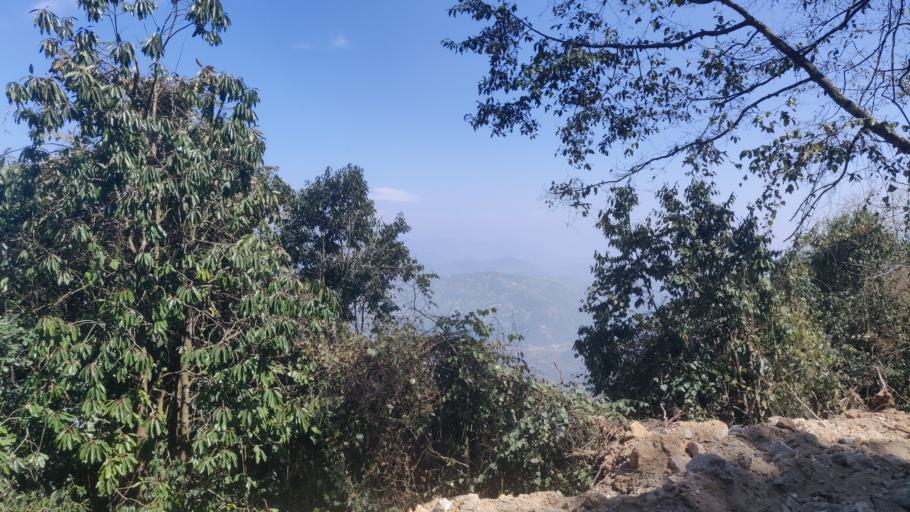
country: NP
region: Central Region
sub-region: Bagmati Zone
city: Nagarkot
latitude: 27.7837
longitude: 85.4822
